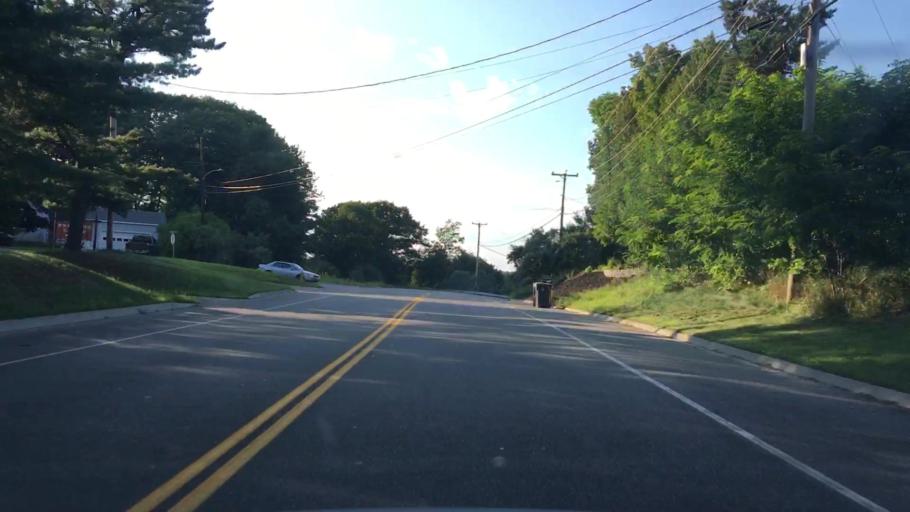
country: US
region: Maine
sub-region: Cumberland County
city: Scarborough
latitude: 43.5933
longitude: -70.2977
